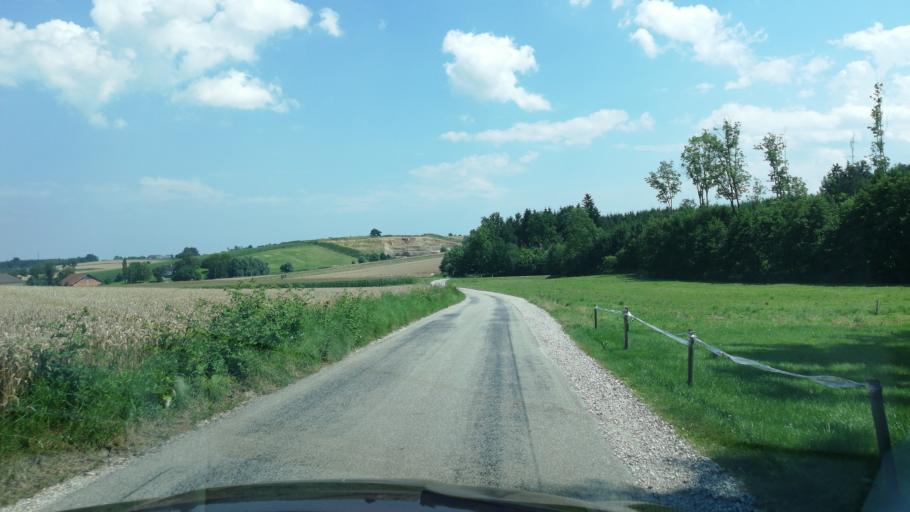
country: AT
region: Upper Austria
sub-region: Wels-Land
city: Buchkirchen
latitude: 48.2177
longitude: 14.0083
